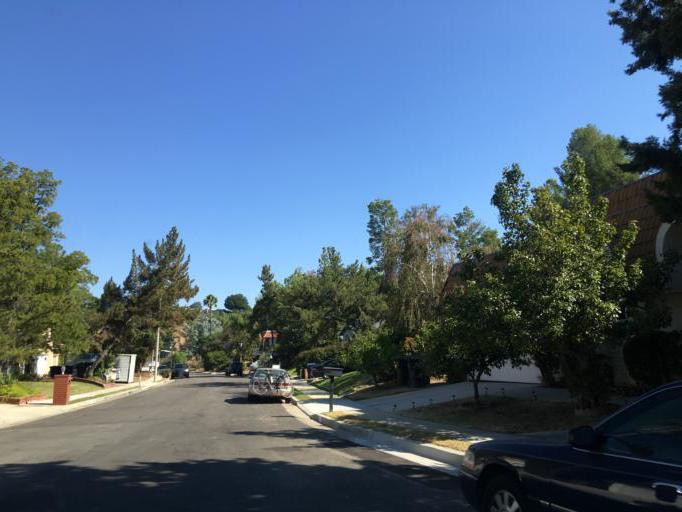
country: US
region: California
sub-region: Los Angeles County
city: Woodland Hills
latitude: 34.1337
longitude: -118.5980
